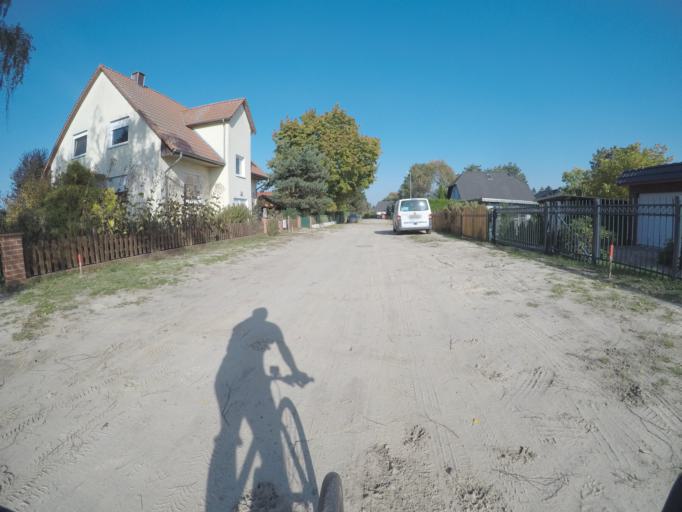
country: DE
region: Brandenburg
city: Oranienburg
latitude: 52.7355
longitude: 13.2520
